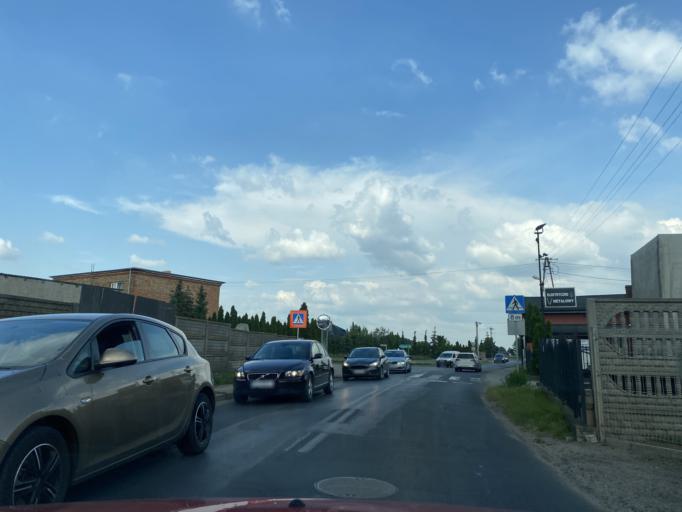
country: PL
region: Greater Poland Voivodeship
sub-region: Powiat poznanski
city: Dopiewo
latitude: 52.3670
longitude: 16.7356
